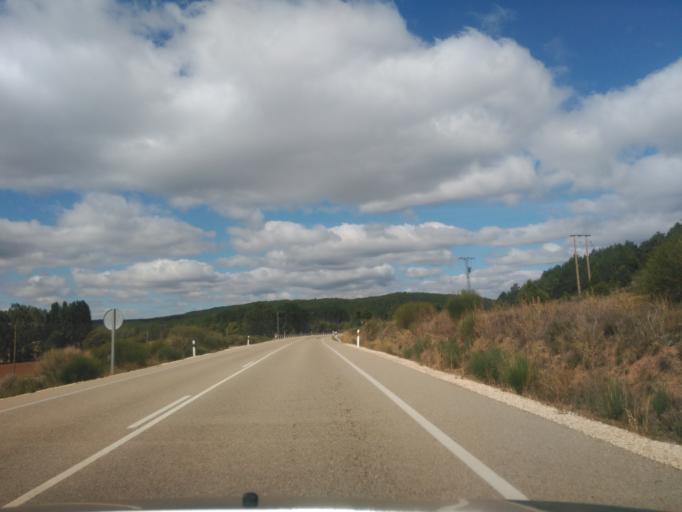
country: ES
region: Castille and Leon
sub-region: Provincia de Burgos
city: Hontoria del Pinar
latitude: 41.8548
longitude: -3.1891
